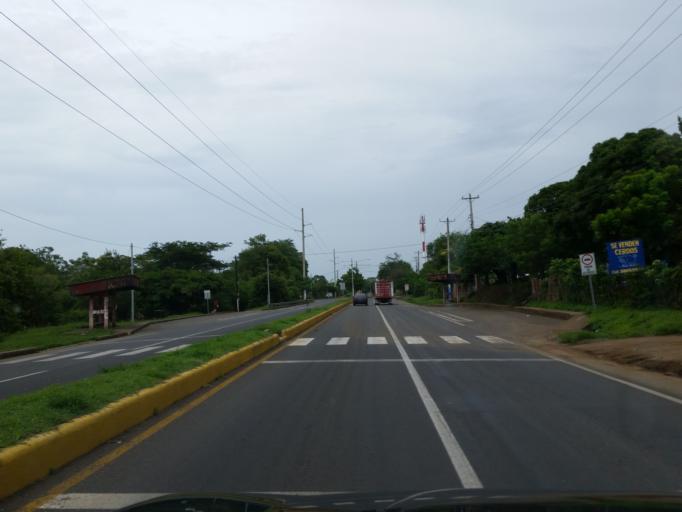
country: NI
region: Masaya
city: Masaya
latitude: 11.9772
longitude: -86.0479
